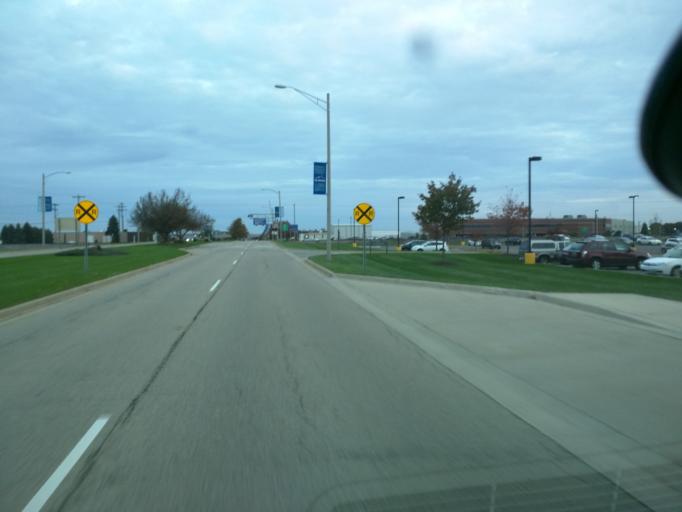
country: US
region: Michigan
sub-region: Ingham County
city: Edgemont Park
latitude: 42.7688
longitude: -84.5888
